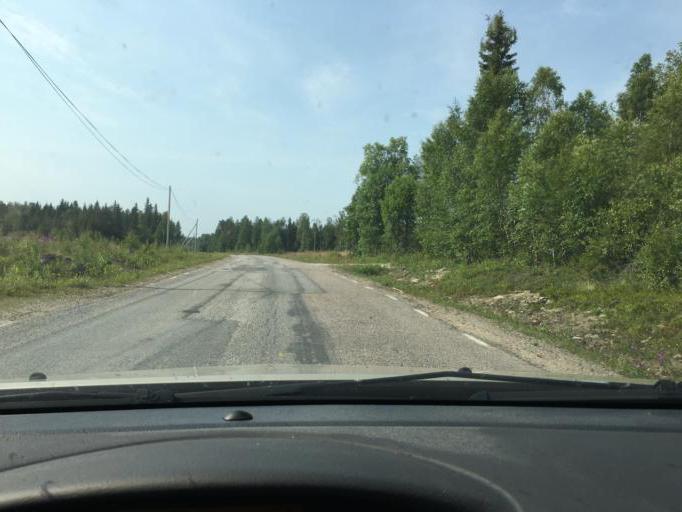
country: SE
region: Norrbotten
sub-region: Kalix Kommun
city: Rolfs
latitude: 65.7732
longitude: 22.9842
